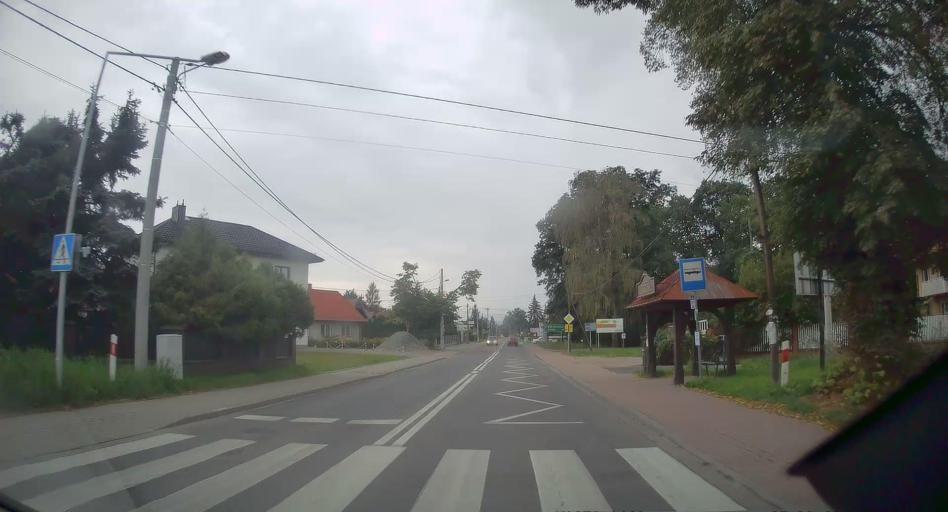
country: PL
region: Lesser Poland Voivodeship
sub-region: Powiat wielicki
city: Niepolomice
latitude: 50.0291
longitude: 20.2062
